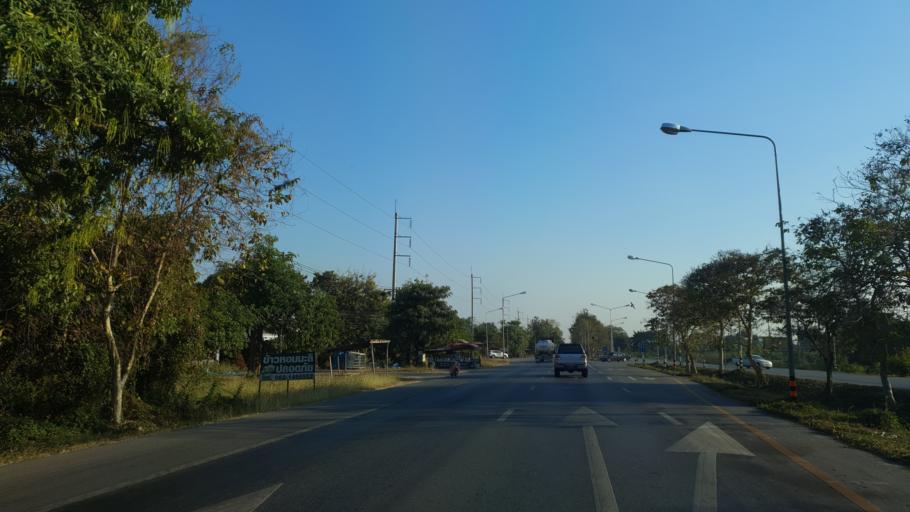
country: TH
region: Kamphaeng Phet
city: Khlong Khlung
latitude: 16.2369
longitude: 99.6950
